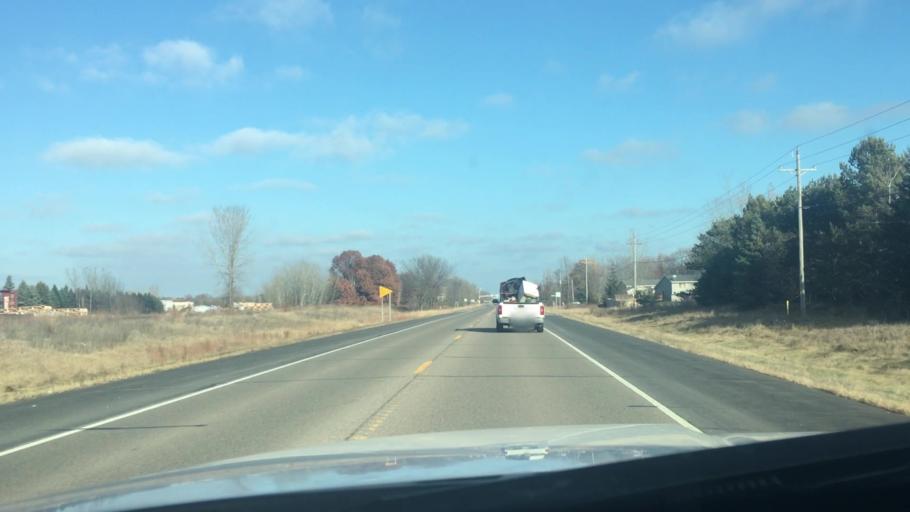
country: US
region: Minnesota
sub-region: Washington County
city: Hugo
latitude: 45.1465
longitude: -92.9971
